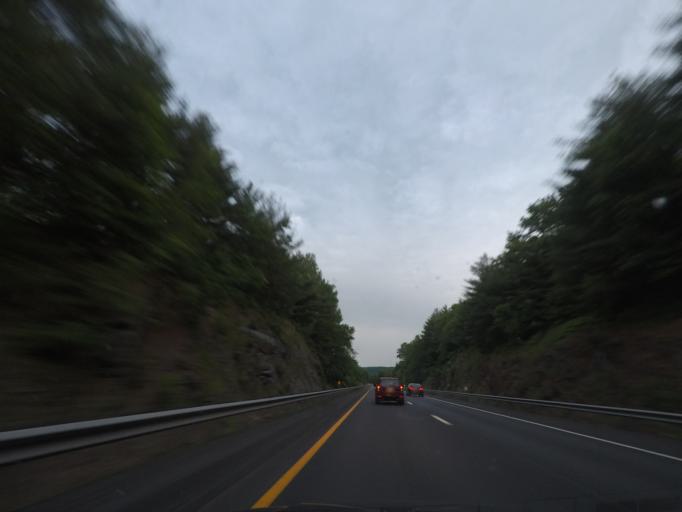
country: US
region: New York
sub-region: Rensselaer County
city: Nassau
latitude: 42.4508
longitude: -73.5737
